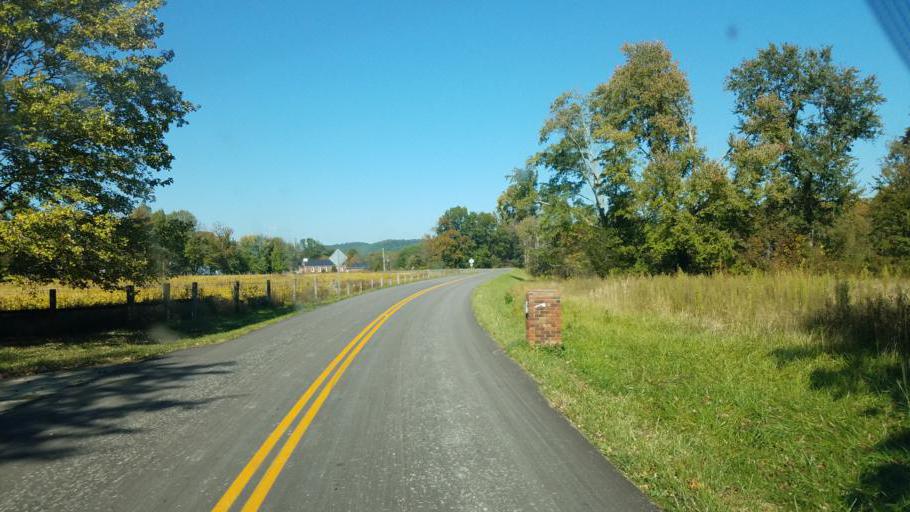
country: US
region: Kentucky
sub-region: Fleming County
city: Flemingsburg
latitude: 38.4493
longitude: -83.5831
